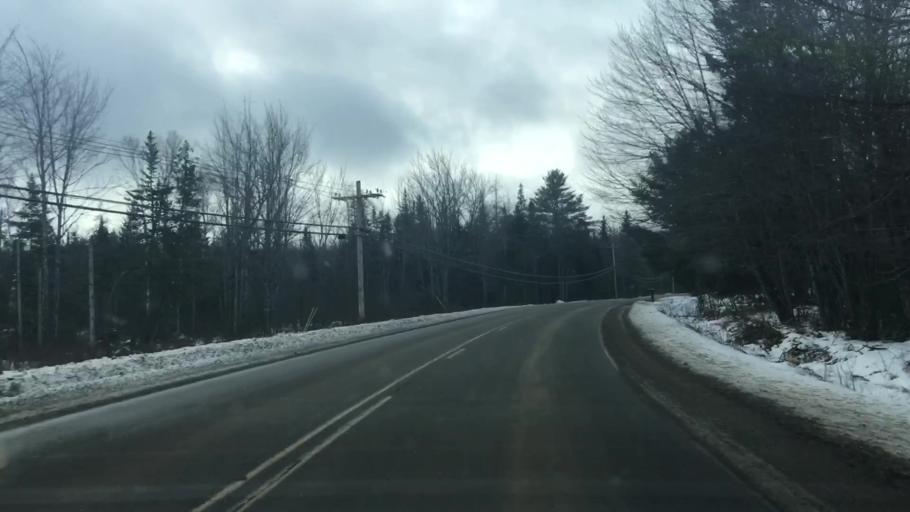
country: US
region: Maine
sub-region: Washington County
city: Calais
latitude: 45.0423
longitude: -67.3278
